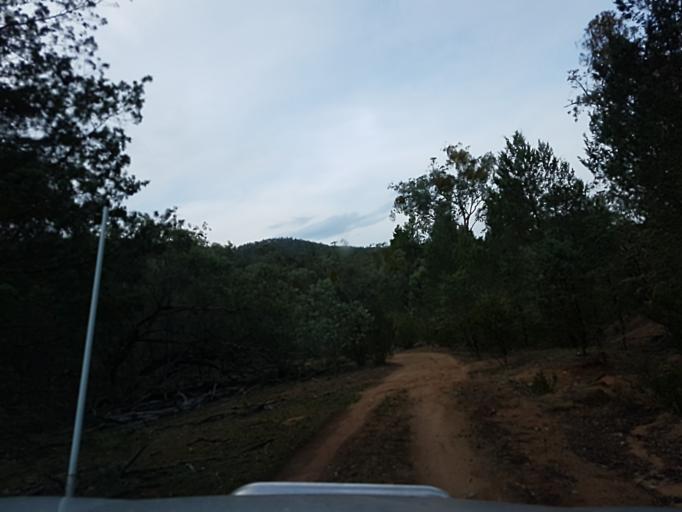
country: AU
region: New South Wales
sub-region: Snowy River
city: Jindabyne
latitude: -36.9449
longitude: 148.3831
